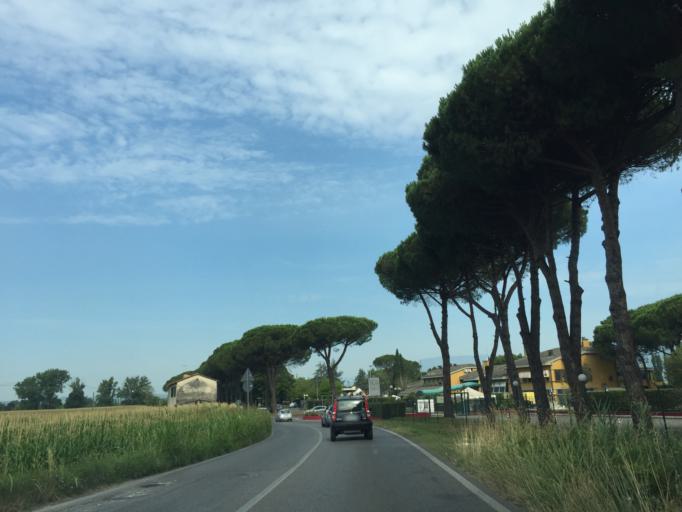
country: IT
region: Tuscany
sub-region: Provincia di Pistoia
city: Montecatini-Terme
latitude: 43.8573
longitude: 10.7716
